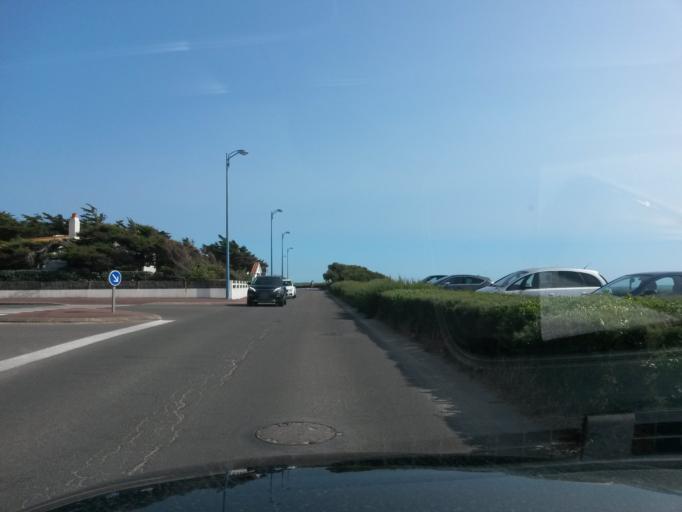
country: FR
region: Pays de la Loire
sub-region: Departement de la Vendee
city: Bretignolles-sur-Mer
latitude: 46.6182
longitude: -1.8708
